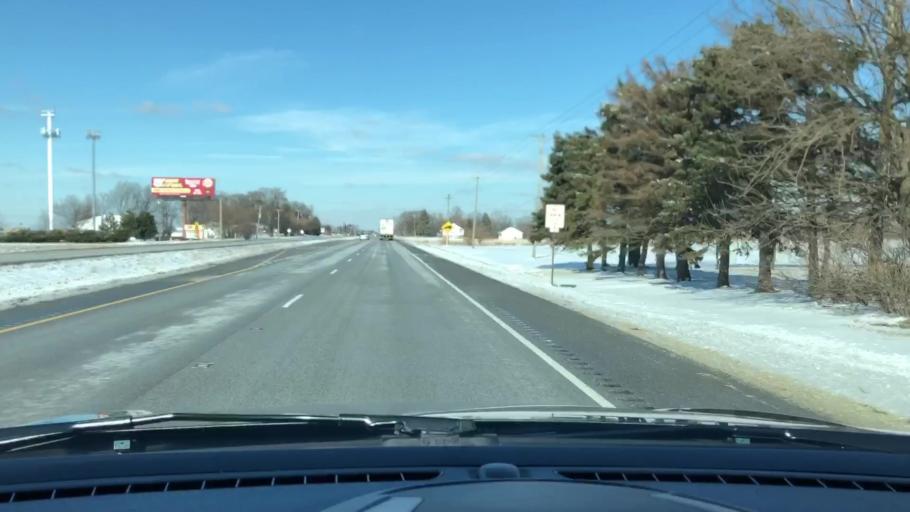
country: US
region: Illinois
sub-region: Will County
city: Preston Heights
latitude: 41.4719
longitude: -88.0797
